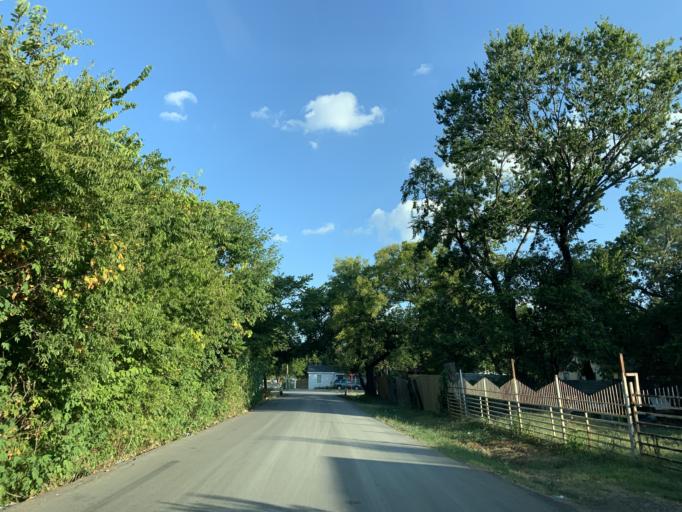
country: US
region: Texas
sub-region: Dallas County
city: Dallas
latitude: 32.6991
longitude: -96.7844
